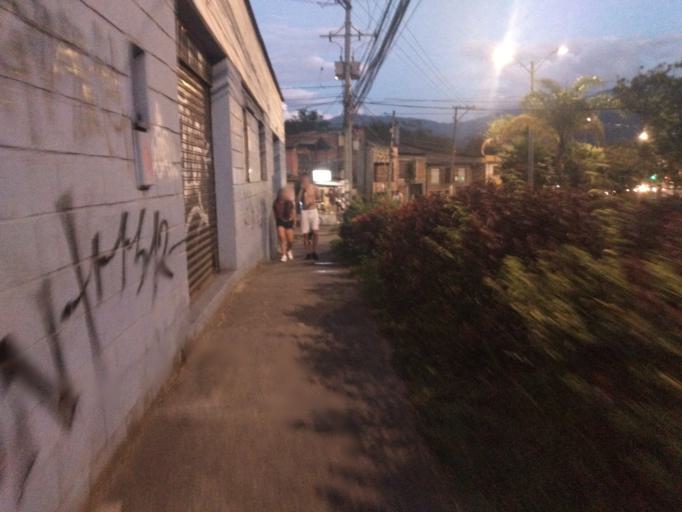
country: CO
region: Antioquia
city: La Estrella
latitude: 6.1722
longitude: -75.6286
